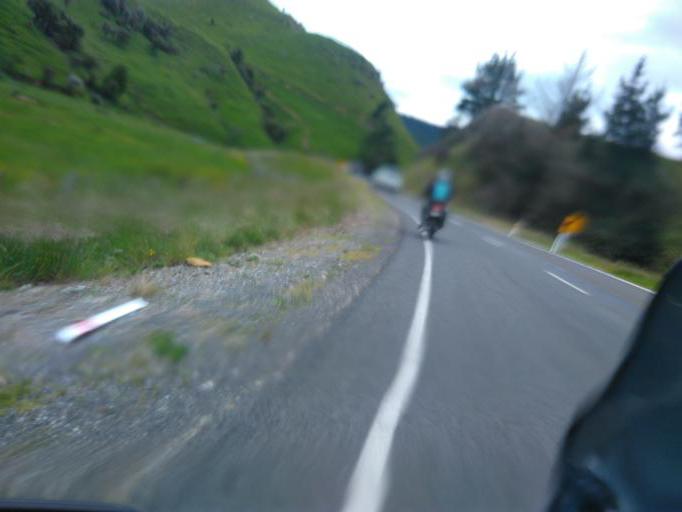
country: NZ
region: Bay of Plenty
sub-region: Opotiki District
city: Opotiki
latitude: -38.3742
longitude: 177.4648
